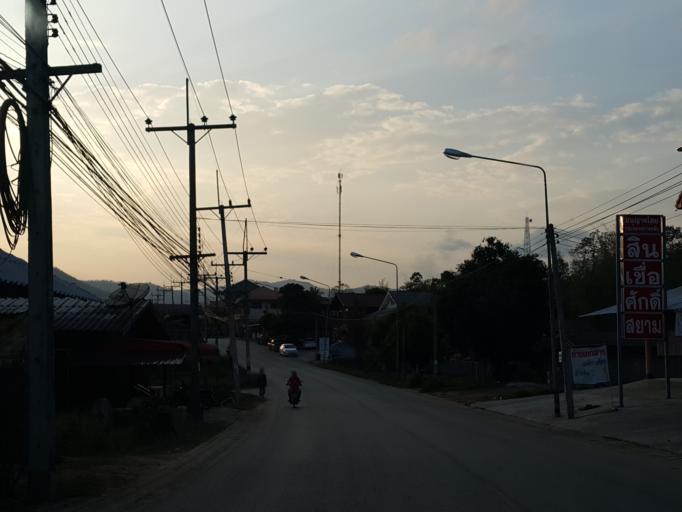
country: TH
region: Lampang
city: Mueang Pan
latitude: 18.7645
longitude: 99.5093
